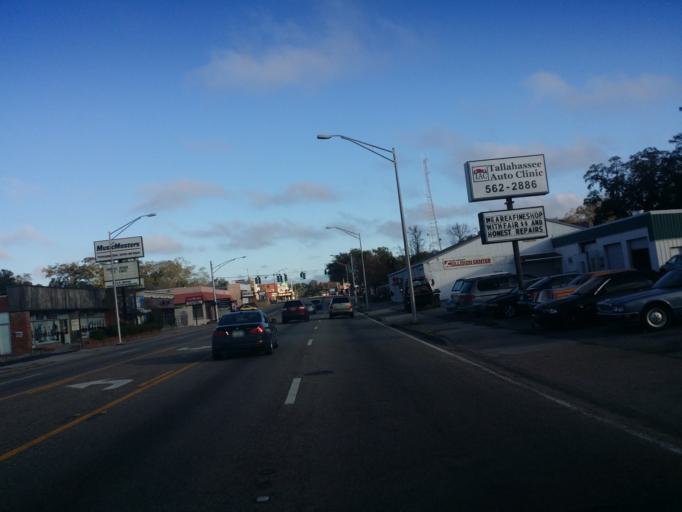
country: US
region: Florida
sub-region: Leon County
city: Tallahassee
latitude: 30.4538
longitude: -84.2807
